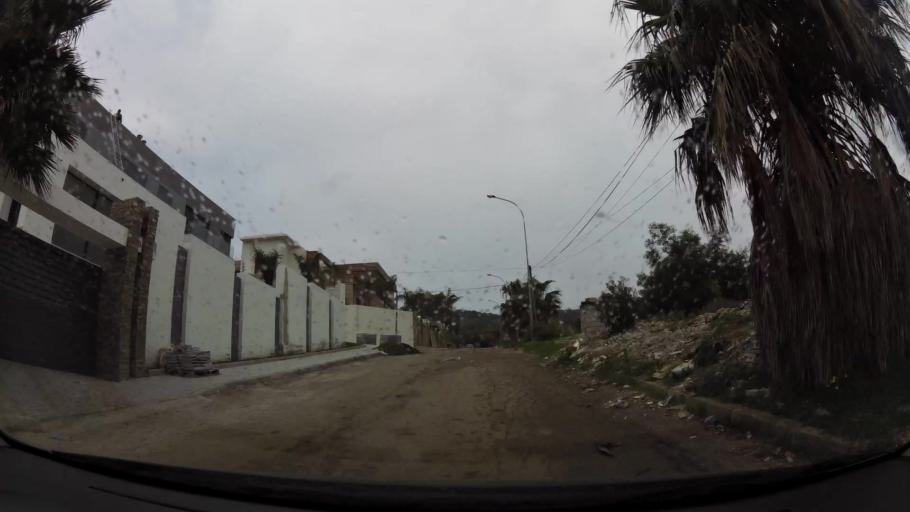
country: MA
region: Tanger-Tetouan
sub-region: Tanger-Assilah
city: Boukhalef
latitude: 35.7788
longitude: -5.8655
